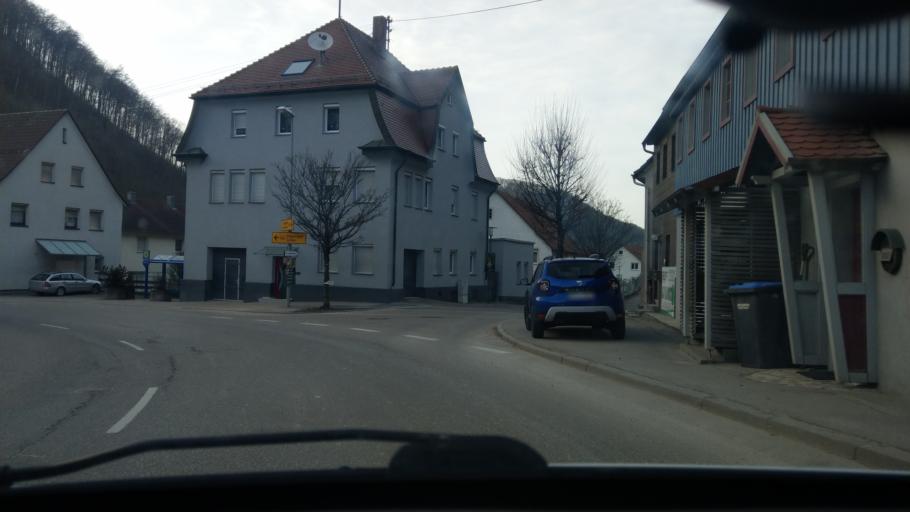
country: DE
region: Baden-Wuerttemberg
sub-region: Regierungsbezirk Stuttgart
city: Bohmenkirch
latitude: 48.7051
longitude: 9.8880
